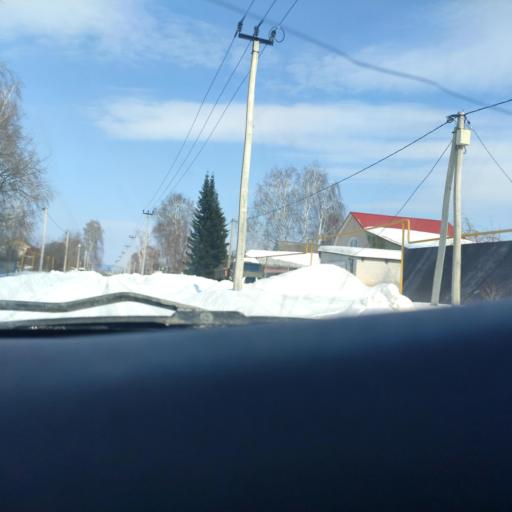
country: RU
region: Samara
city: Rozhdestveno
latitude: 53.2414
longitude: 50.0614
